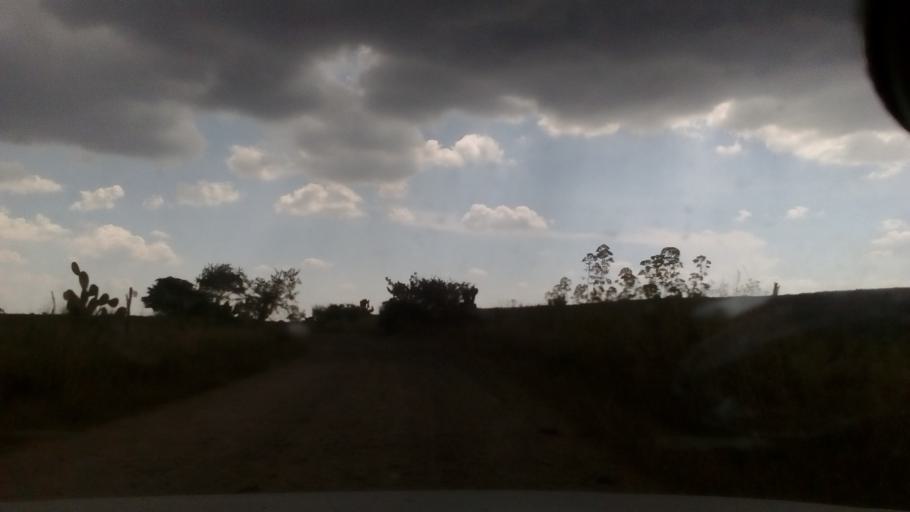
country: MX
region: Guanajuato
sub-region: Silao de la Victoria
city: San Francisco (Banos de Agua Caliente)
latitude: 21.1842
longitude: -101.4177
